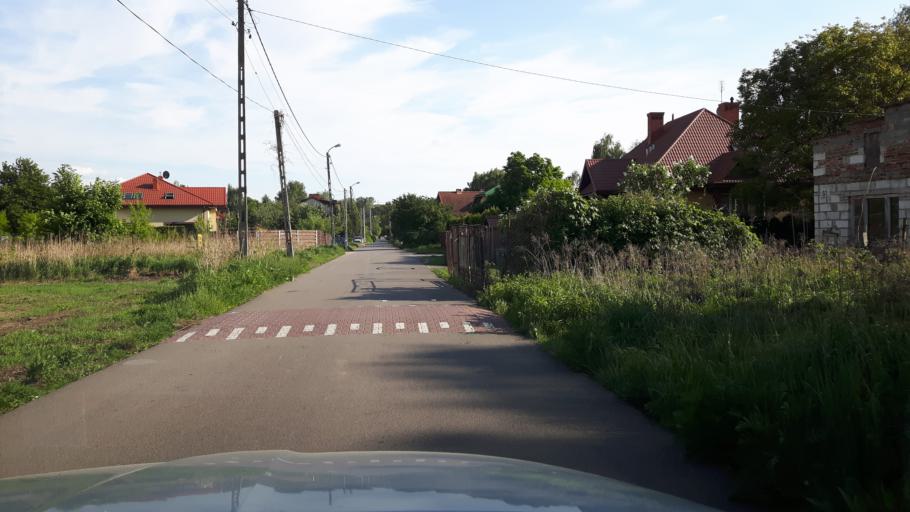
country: PL
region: Masovian Voivodeship
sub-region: Warszawa
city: Praga Poludnie
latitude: 52.2567
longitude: 21.1208
